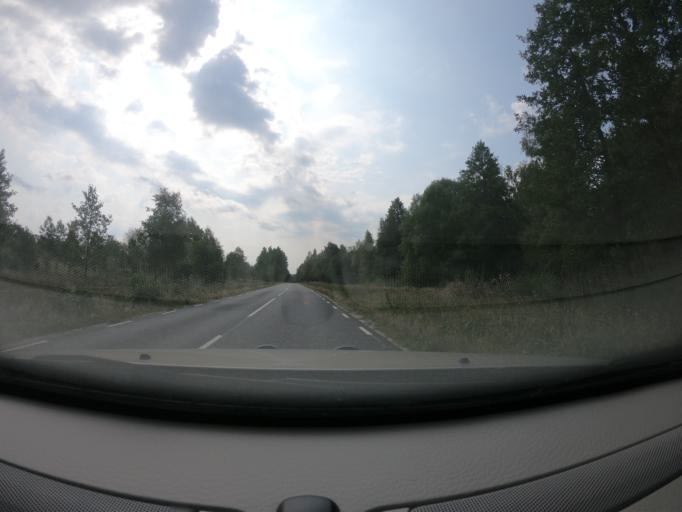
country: SE
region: Kronoberg
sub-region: Vaxjo Kommun
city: Braas
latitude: 57.1652
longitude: 14.9602
